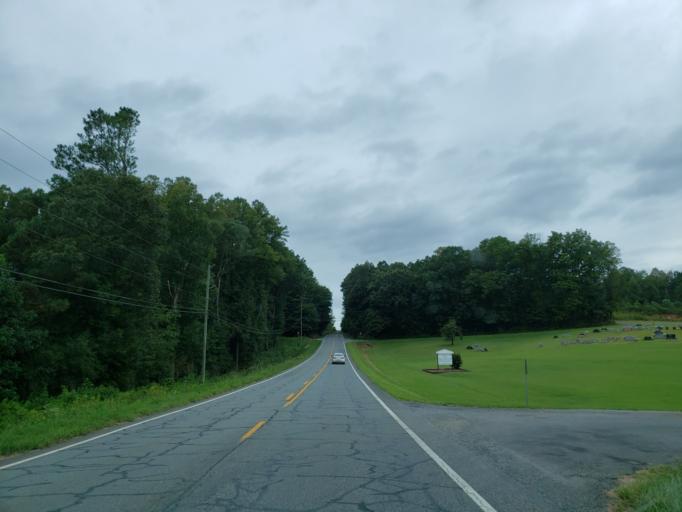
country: US
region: Georgia
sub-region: Gilmer County
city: Ellijay
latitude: 34.6412
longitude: -84.5609
